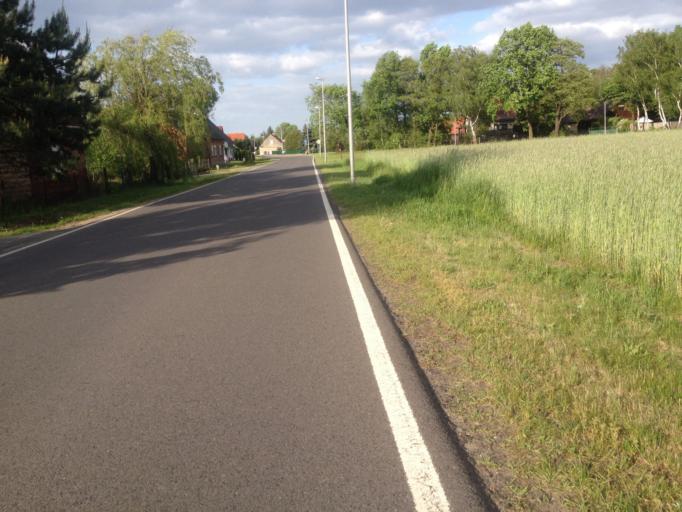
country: DE
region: Brandenburg
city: Cottbus
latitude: 51.8150
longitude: 14.3362
